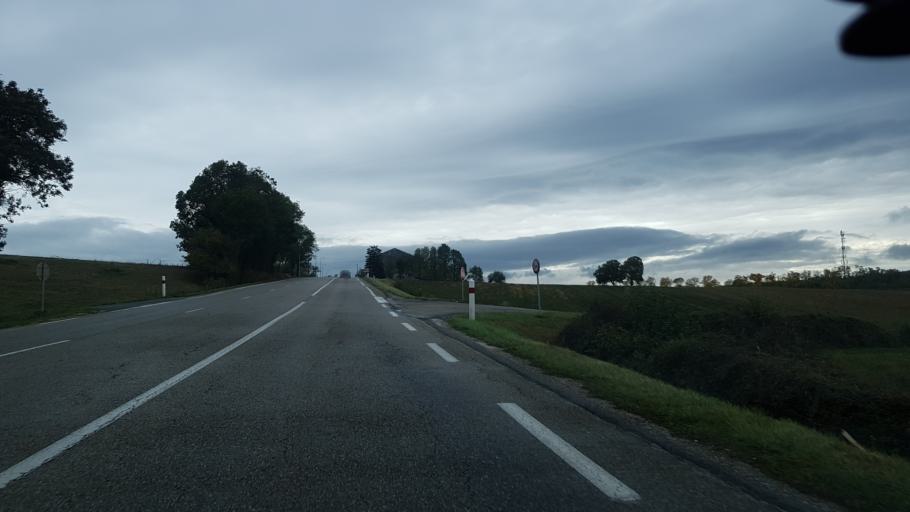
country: FR
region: Rhone-Alpes
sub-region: Departement de l'Ain
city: Saint-Martin-du-Mont
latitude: 46.0757
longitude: 5.3224
